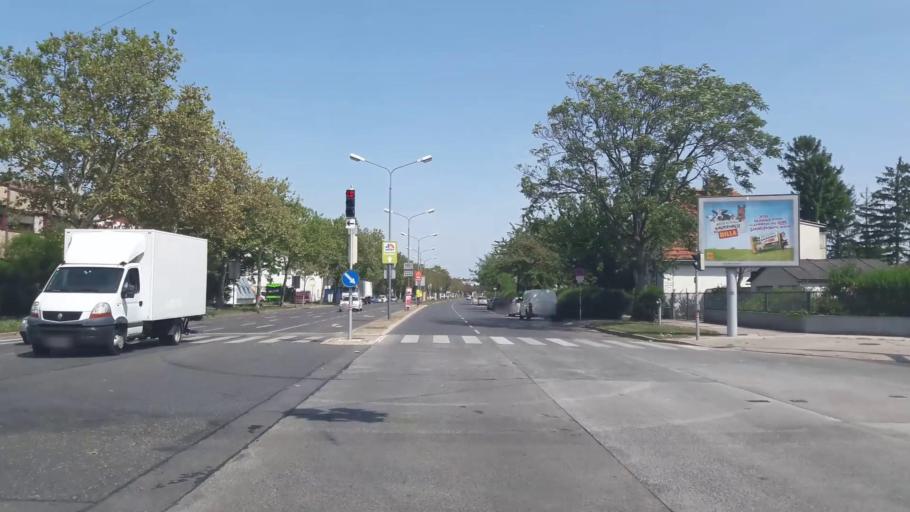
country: AT
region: Lower Austria
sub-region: Politischer Bezirk Modling
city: Vosendorf
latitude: 48.1396
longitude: 16.3588
